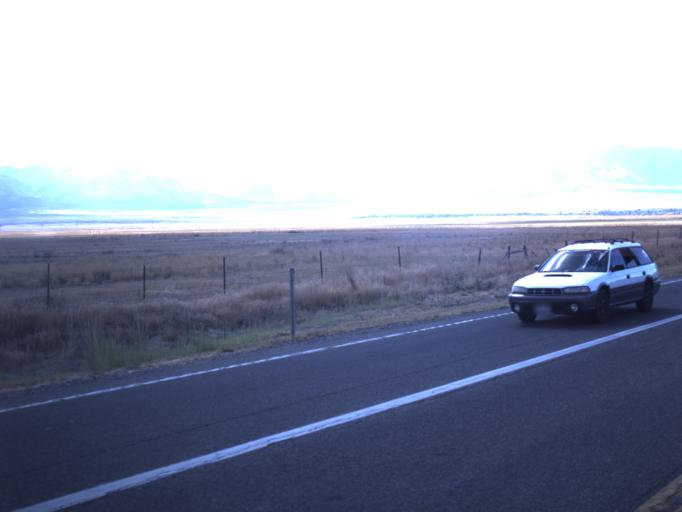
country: US
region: Utah
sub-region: Tooele County
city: Erda
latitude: 40.5703
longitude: -112.3751
